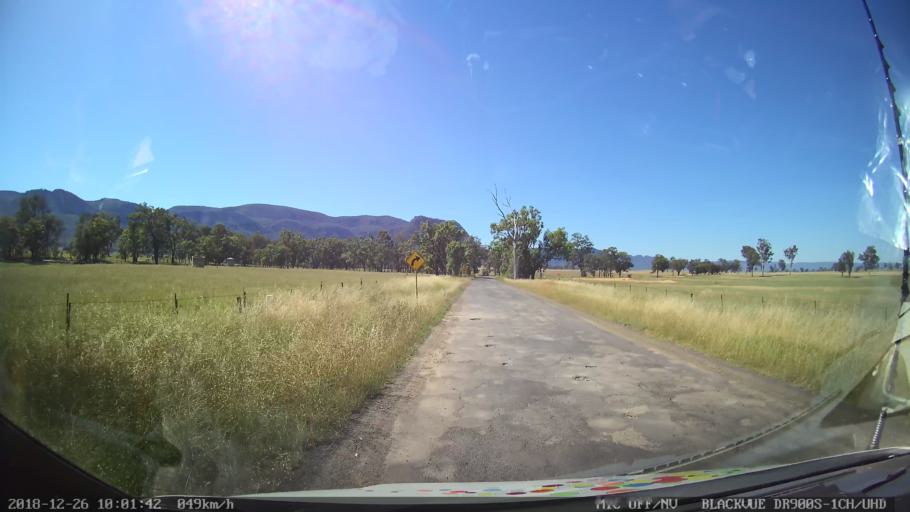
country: AU
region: New South Wales
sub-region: Mid-Western Regional
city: Kandos
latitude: -33.0490
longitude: 150.2226
